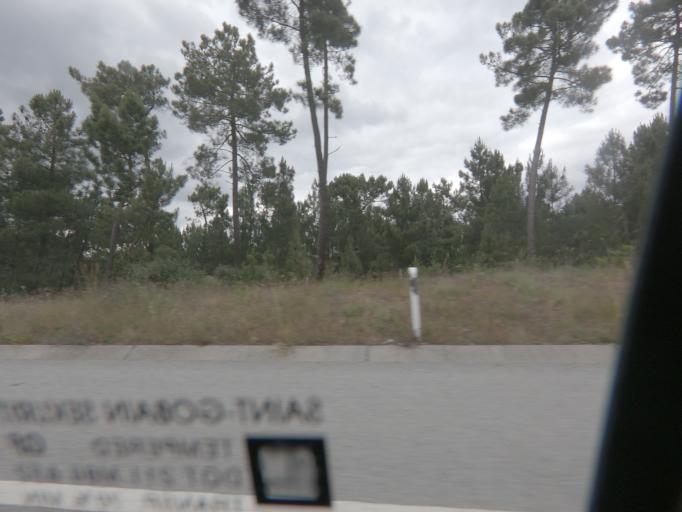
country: PT
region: Vila Real
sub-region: Sabrosa
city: Vilela
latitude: 41.2672
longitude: -7.6451
